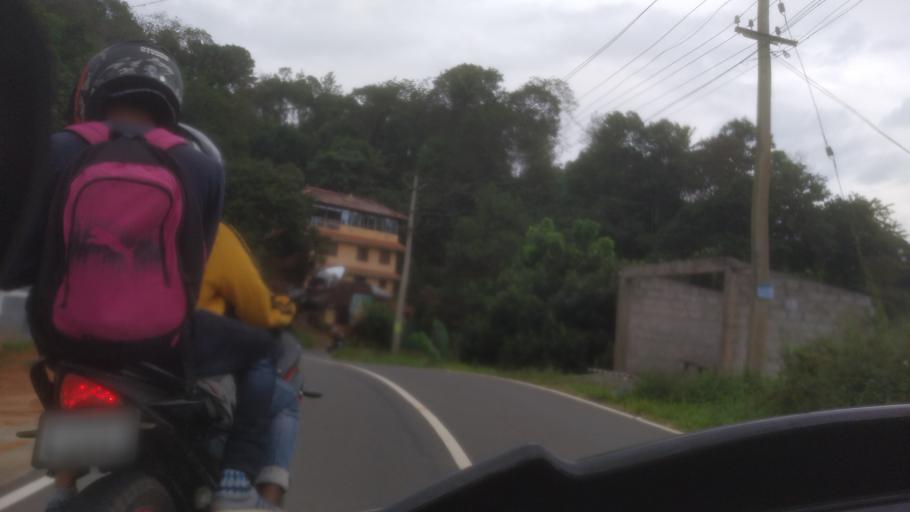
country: IN
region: Kerala
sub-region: Idukki
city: Idukki
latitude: 9.9480
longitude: 77.0129
